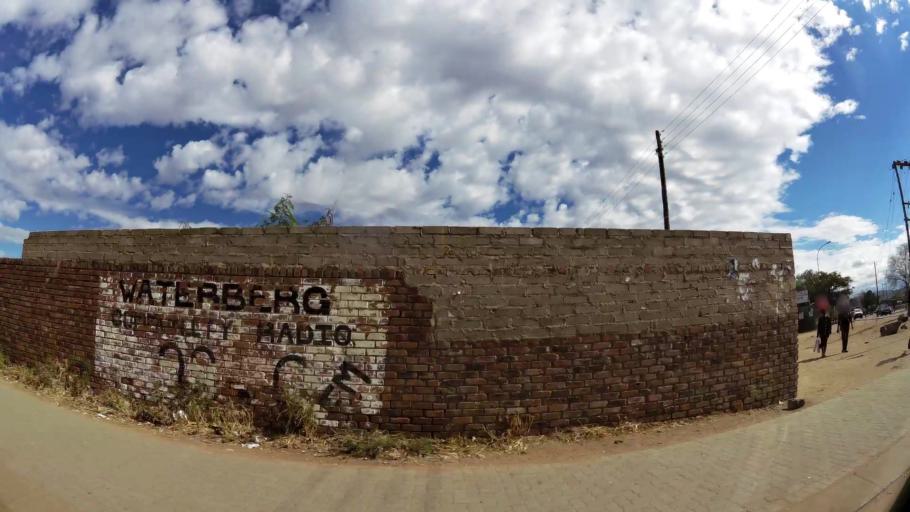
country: ZA
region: Limpopo
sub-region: Waterberg District Municipality
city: Bela-Bela
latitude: -24.8862
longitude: 28.3110
